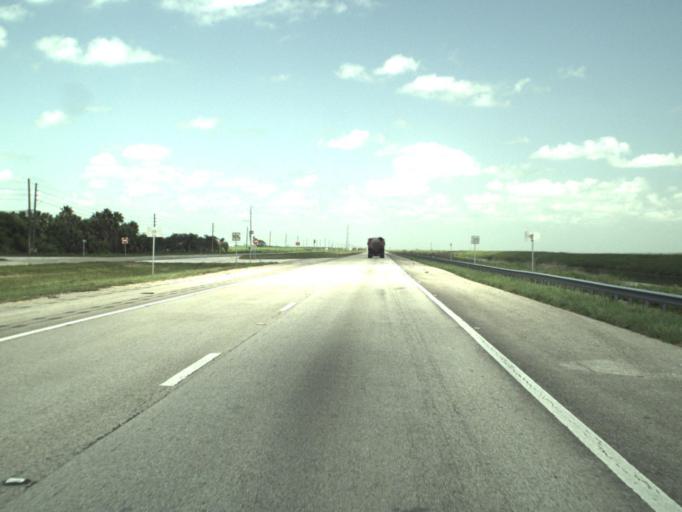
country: US
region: Florida
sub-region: Palm Beach County
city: Belle Glade Camp
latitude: 26.4892
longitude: -80.6571
